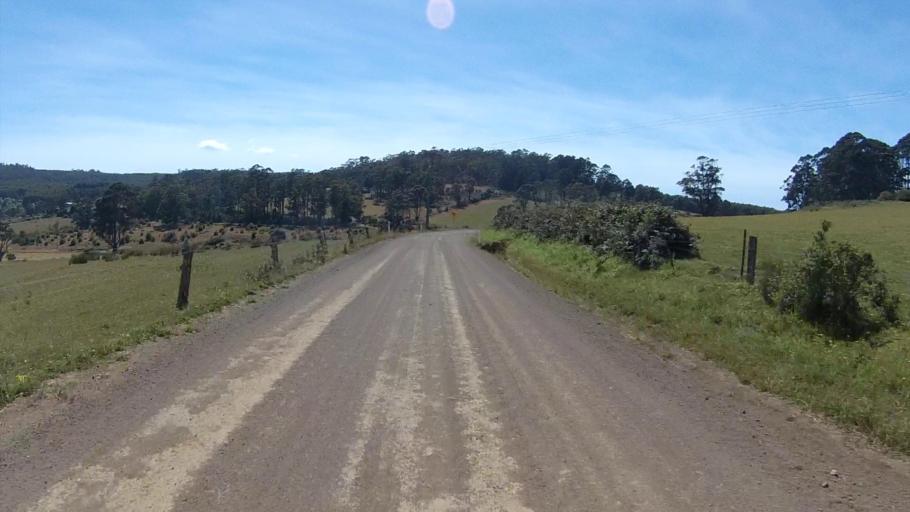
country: AU
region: Tasmania
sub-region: Sorell
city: Sorell
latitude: -42.7209
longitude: 147.7465
